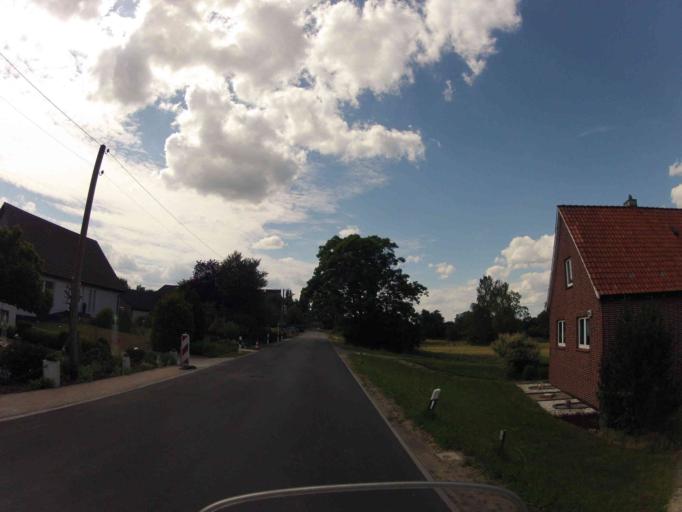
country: DE
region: Lower Saxony
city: Stelle
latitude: 53.4549
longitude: 10.1519
